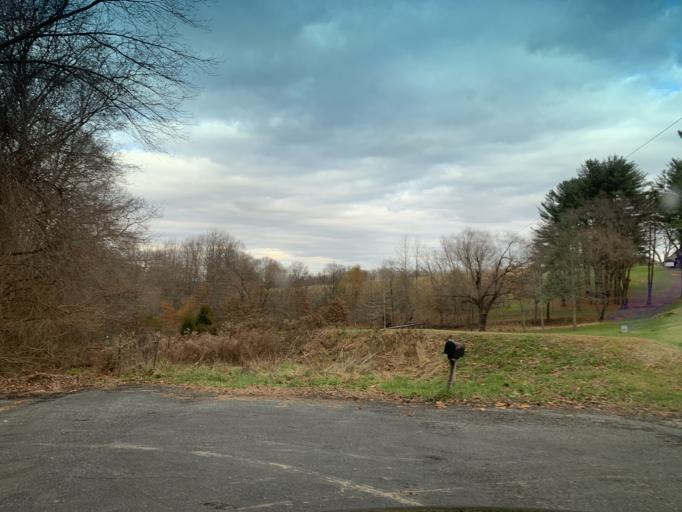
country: US
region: Maryland
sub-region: Harford County
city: Jarrettsville
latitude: 39.6564
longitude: -76.4541
